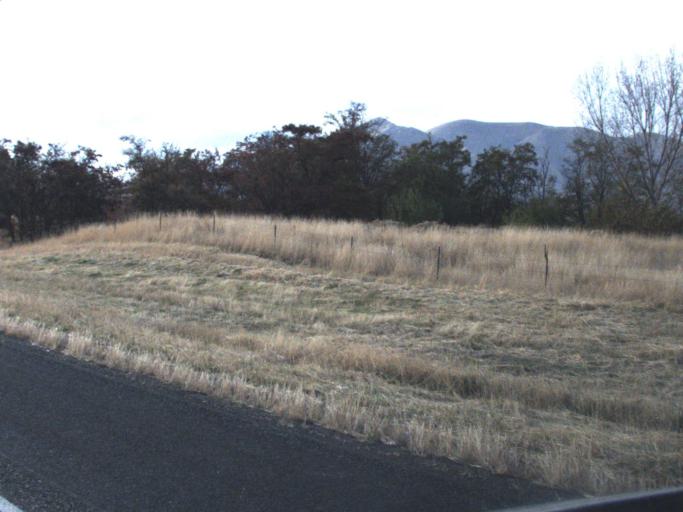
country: US
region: Washington
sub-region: Asotin County
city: Clarkston Heights-Vineland
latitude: 46.4186
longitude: -117.1742
